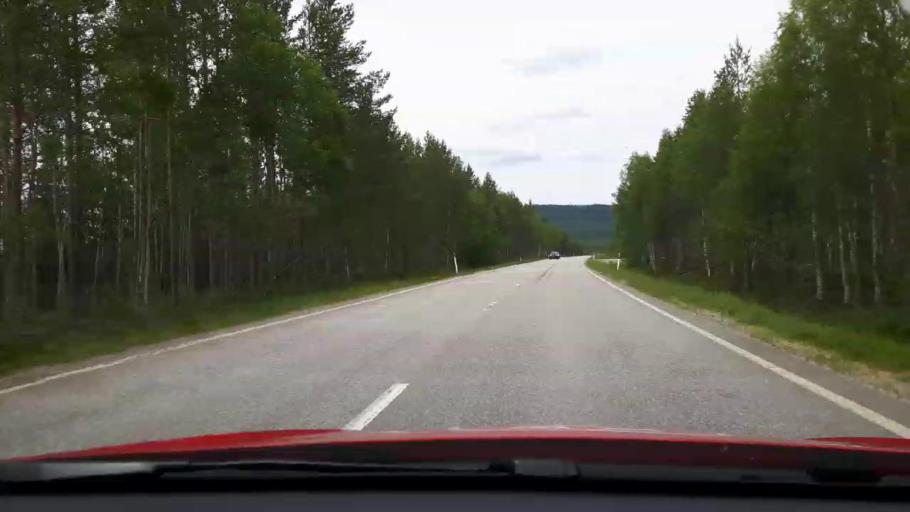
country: SE
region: Jaemtland
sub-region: Harjedalens Kommun
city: Sveg
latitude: 62.0831
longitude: 14.2546
